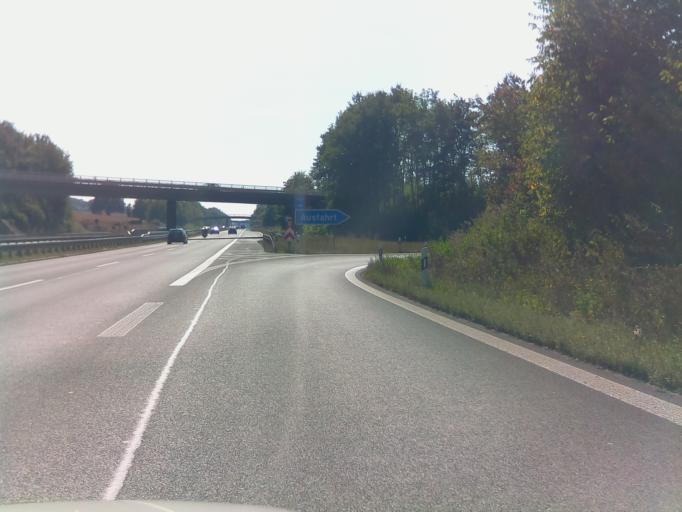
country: DE
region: Bavaria
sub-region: Upper Franconia
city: Bad Staffelstein
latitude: 50.1111
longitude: 11.0151
